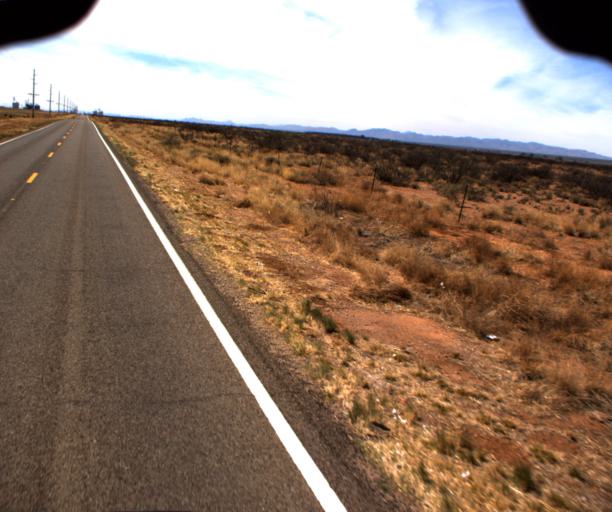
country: US
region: Arizona
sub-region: Cochise County
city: Tombstone
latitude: 31.7861
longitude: -109.6918
